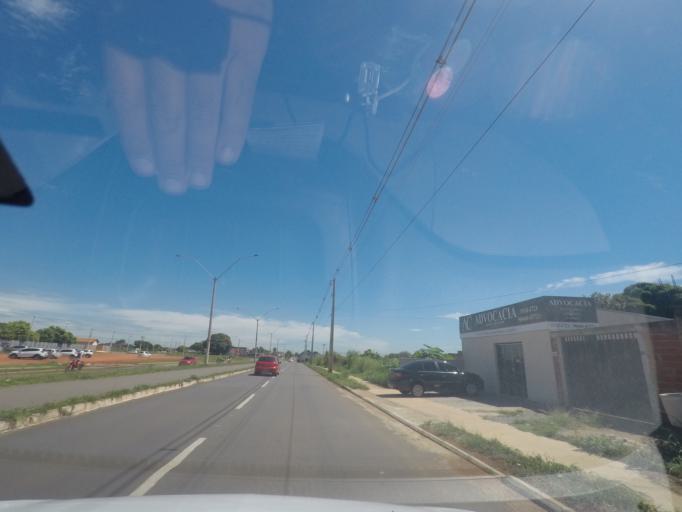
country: BR
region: Goias
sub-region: Aparecida De Goiania
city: Aparecida de Goiania
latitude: -16.7898
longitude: -49.3300
